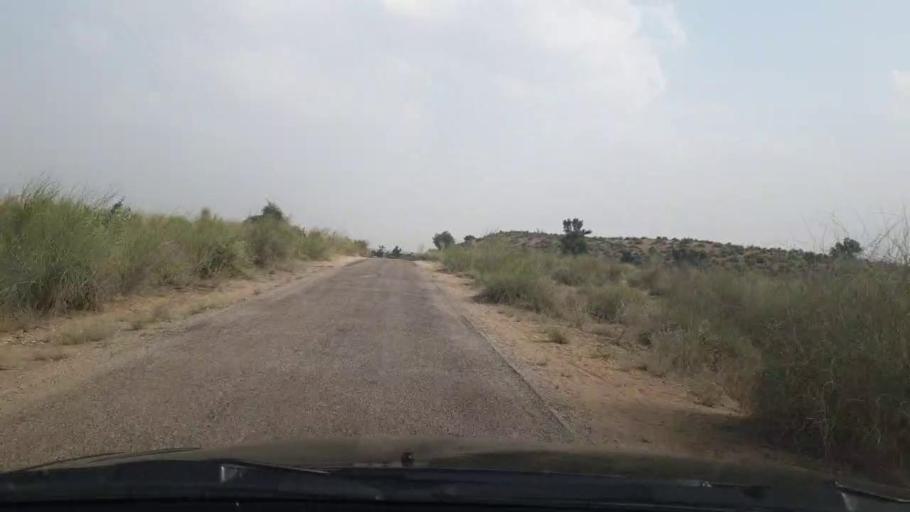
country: PK
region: Sindh
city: Islamkot
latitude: 25.0228
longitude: 70.5901
